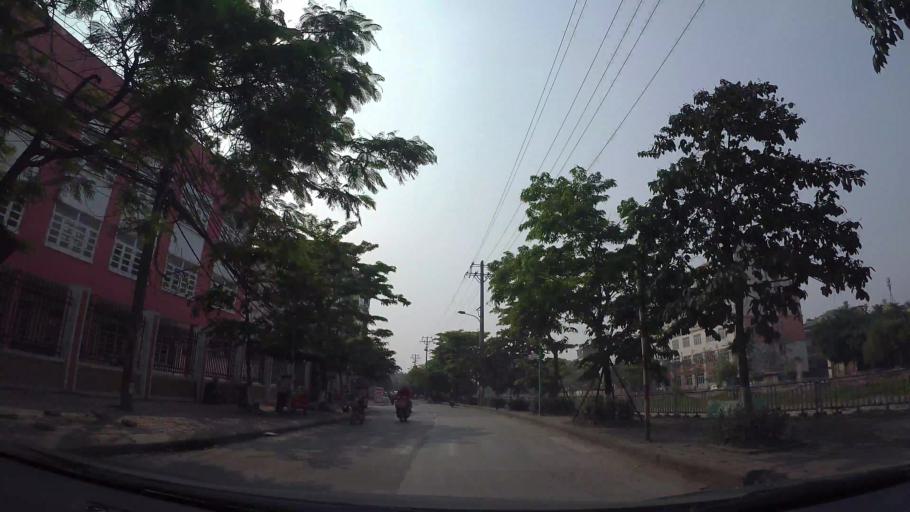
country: VN
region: Ha Noi
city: Thanh Xuan
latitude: 20.9788
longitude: 105.8219
